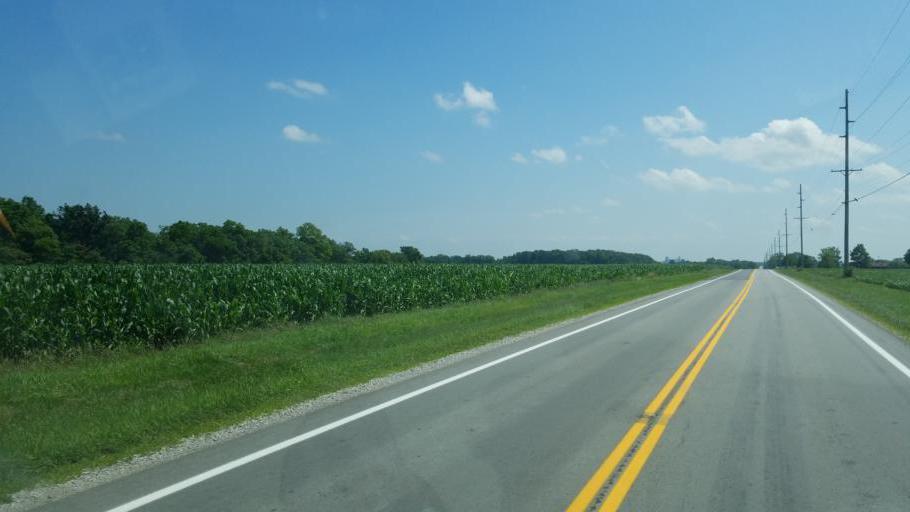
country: US
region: Ohio
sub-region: Huron County
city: Bellevue
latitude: 41.3415
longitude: -82.8303
